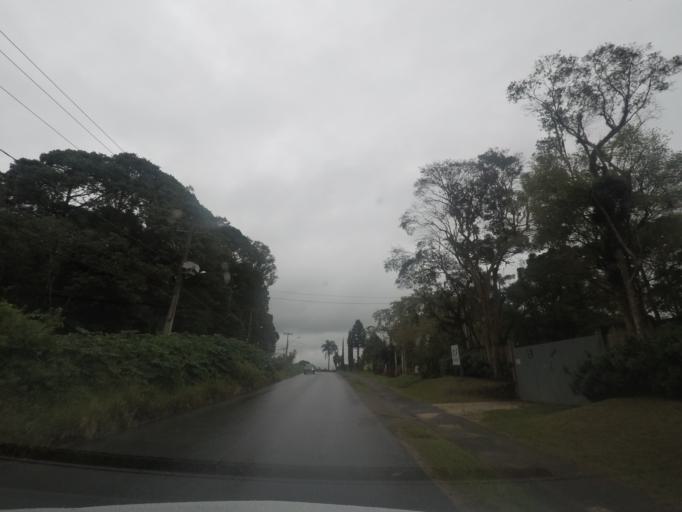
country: BR
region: Parana
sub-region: Quatro Barras
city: Quatro Barras
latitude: -25.3867
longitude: -49.1389
